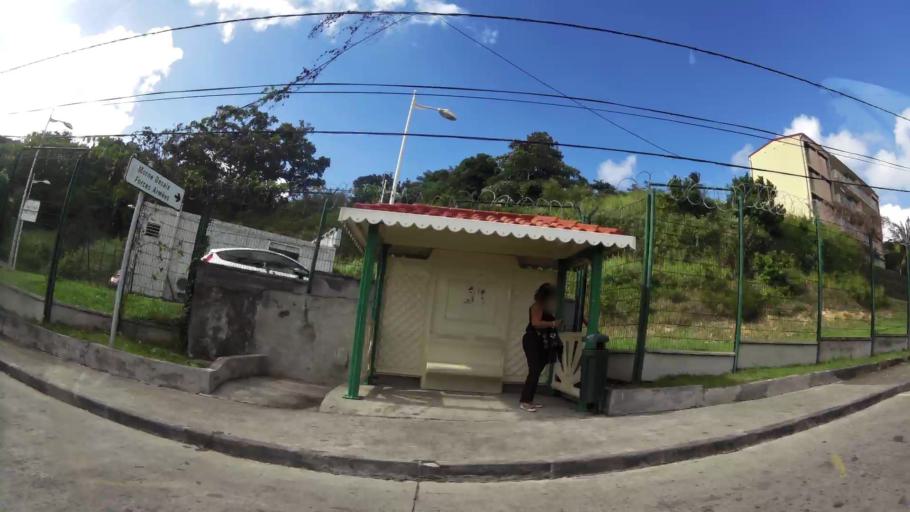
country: MQ
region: Martinique
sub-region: Martinique
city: Fort-de-France
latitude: 14.6180
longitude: -61.0615
